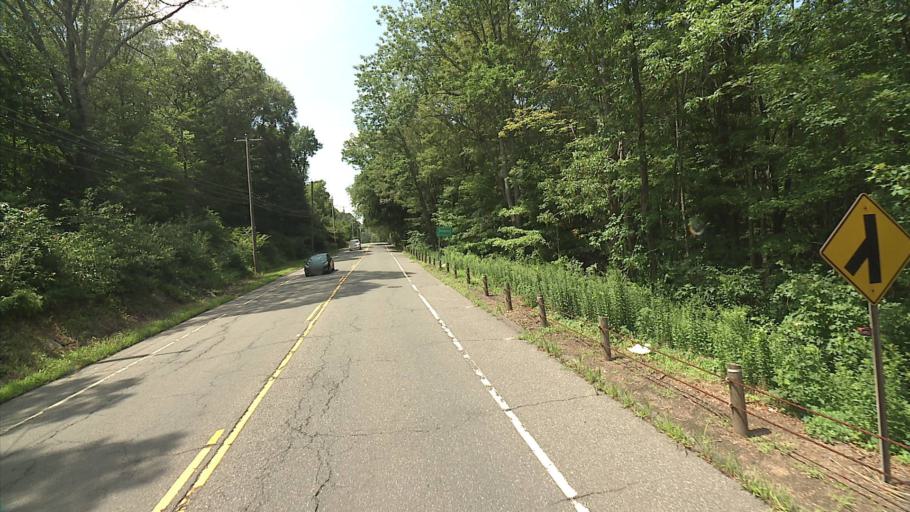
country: US
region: Connecticut
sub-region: Tolland County
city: South Coventry
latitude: 41.7645
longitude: -72.2879
